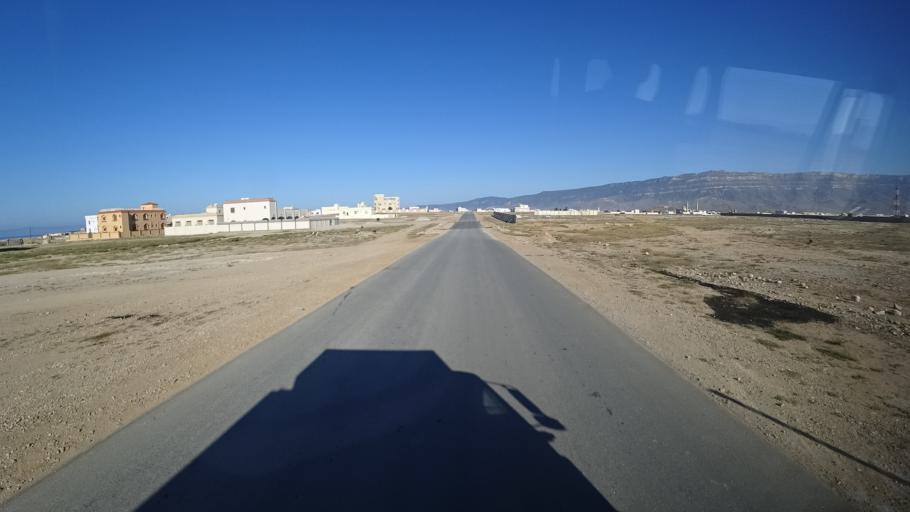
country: OM
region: Zufar
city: Salalah
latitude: 16.9783
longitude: 54.7002
